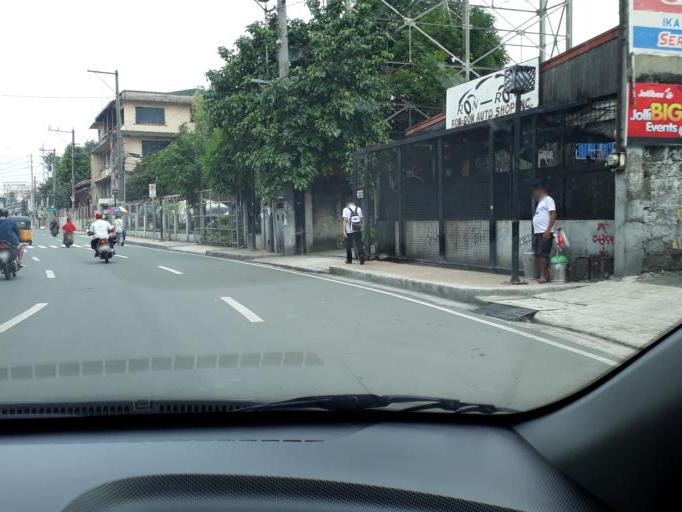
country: PH
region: Metro Manila
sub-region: City of Manila
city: Quiapo
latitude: 14.6000
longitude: 121.0000
